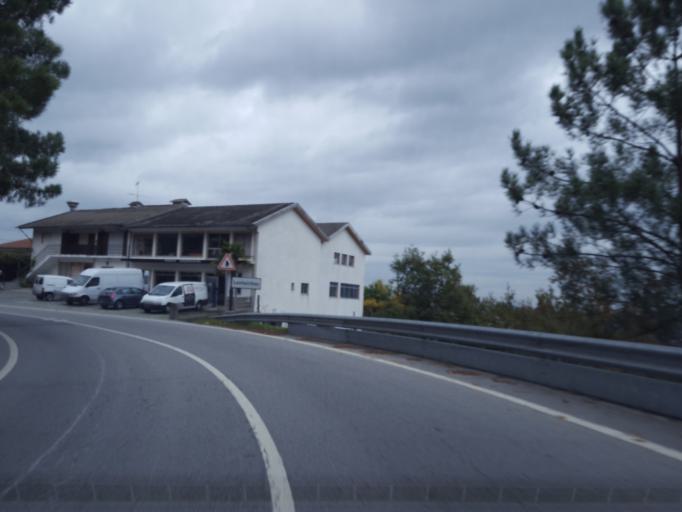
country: PT
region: Porto
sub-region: Marco de Canaveses
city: Marco de Canavezes
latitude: 41.1655
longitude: -8.1446
